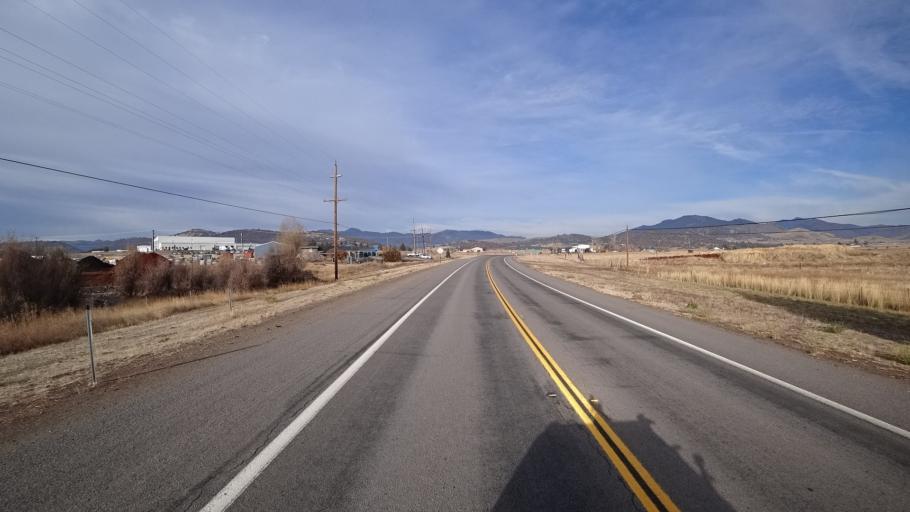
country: US
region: California
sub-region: Siskiyou County
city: Yreka
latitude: 41.7346
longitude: -122.5913
